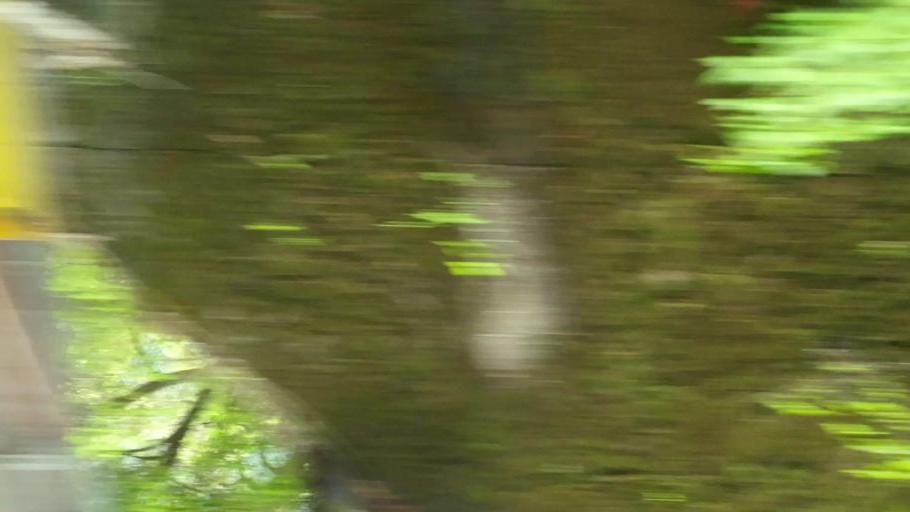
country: JP
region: Tokushima
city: Ikedacho
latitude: 33.9117
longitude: 133.7573
